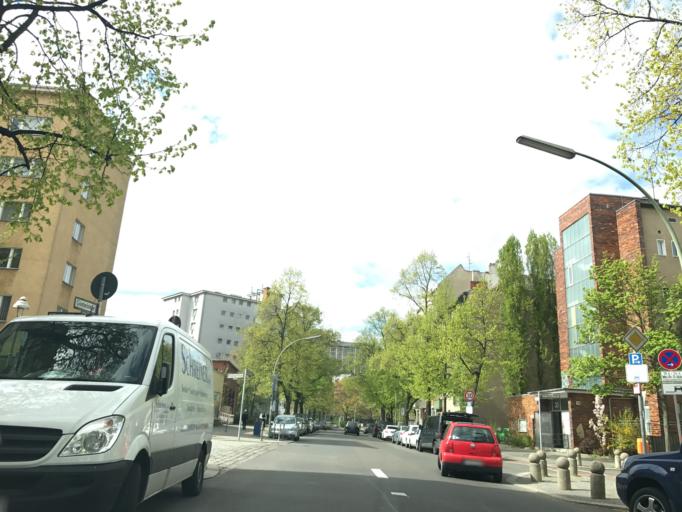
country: DE
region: Berlin
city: Wilmersdorf Bezirk
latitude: 52.4917
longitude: 13.3220
